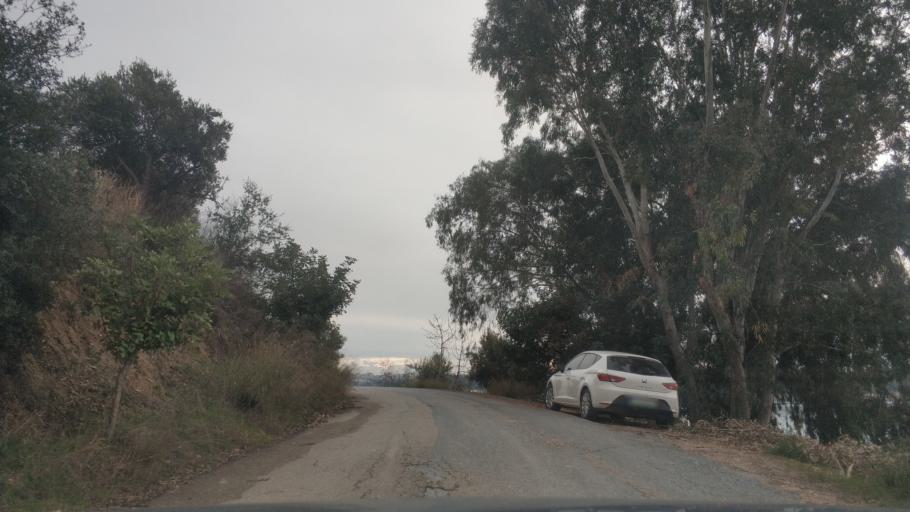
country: TR
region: Adana
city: Adana
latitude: 37.0978
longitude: 35.2882
